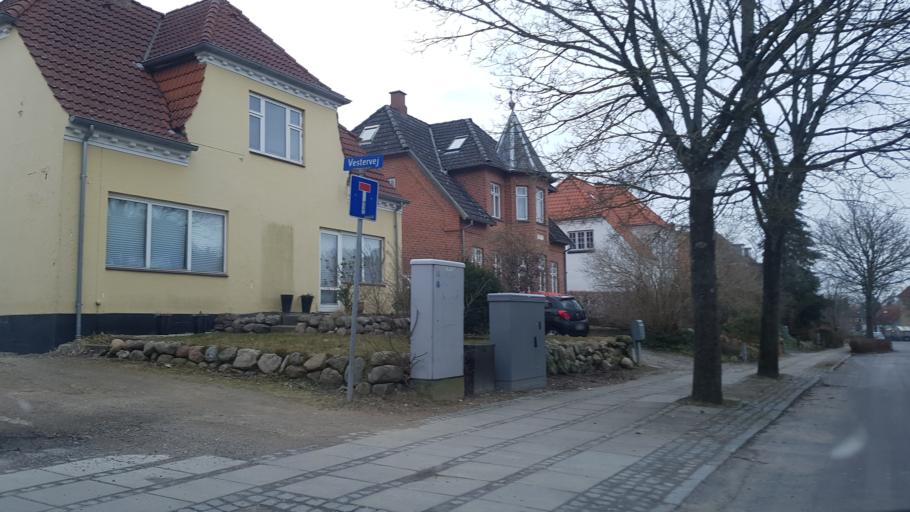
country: DK
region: Zealand
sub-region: Soro Kommune
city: Frederiksberg
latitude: 55.4172
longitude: 11.5674
